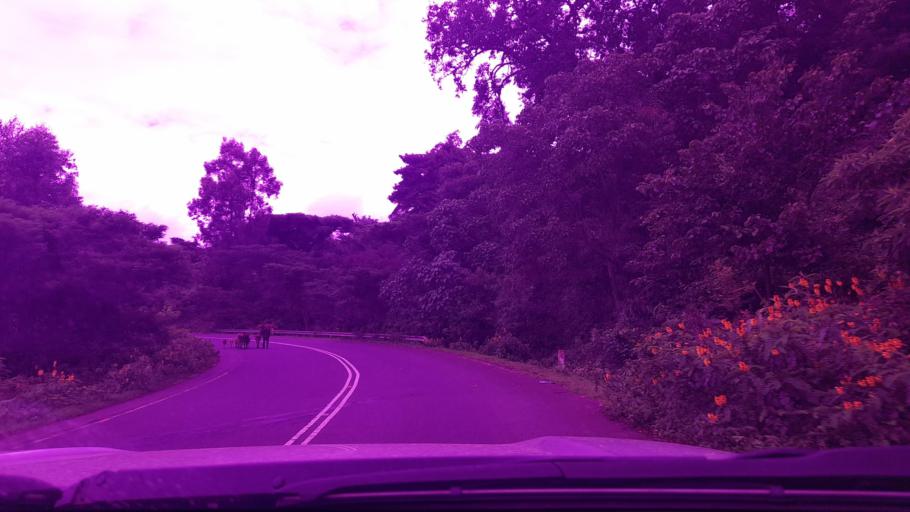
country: ET
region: Oromiya
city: Jima
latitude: 7.5581
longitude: 36.5987
